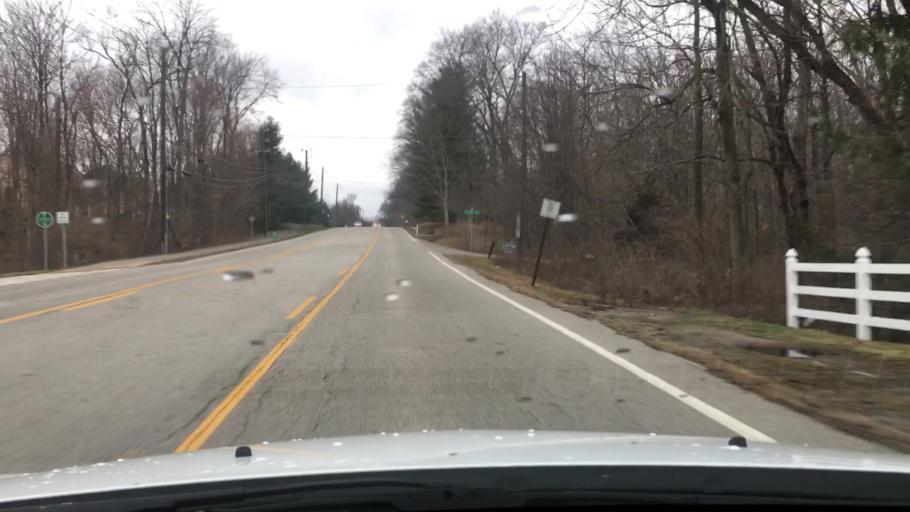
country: US
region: Indiana
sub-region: Boone County
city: Zionsville
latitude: 39.8814
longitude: -86.2786
